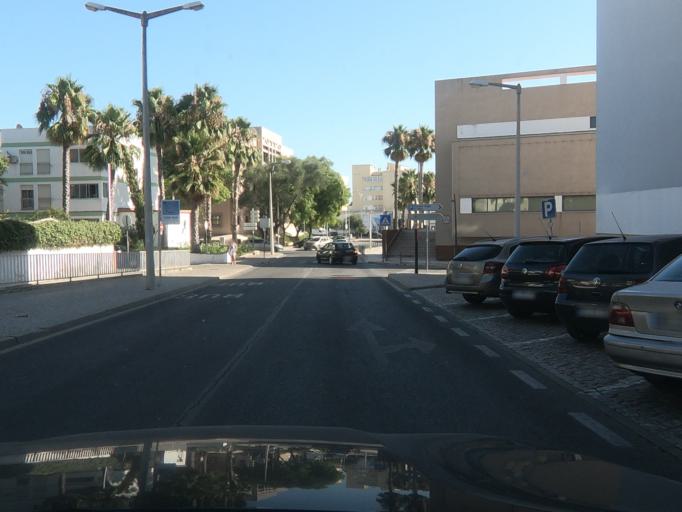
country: PT
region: Faro
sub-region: Loule
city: Loule
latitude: 37.1394
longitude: -8.0180
